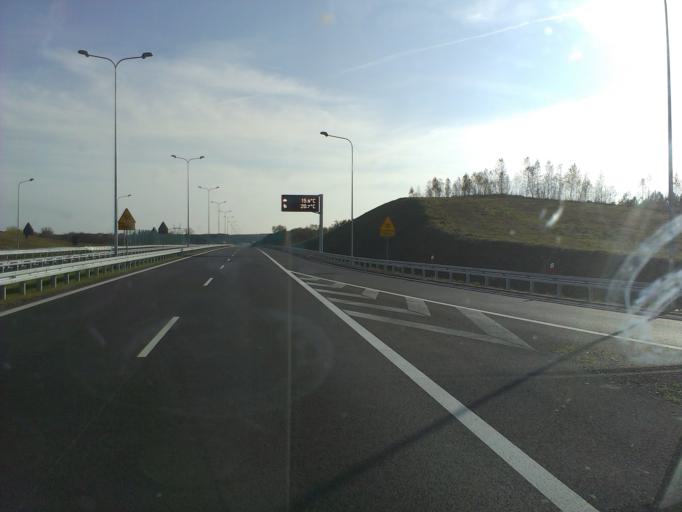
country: PL
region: Lubusz
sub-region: Powiat miedzyrzecki
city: Skwierzyna
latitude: 52.5873
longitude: 15.4489
